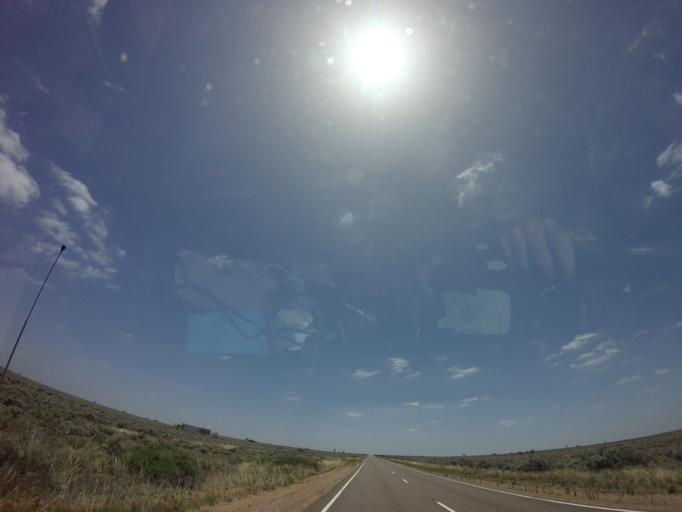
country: AU
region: South Australia
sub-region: Whyalla
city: Whyalla
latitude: -32.8454
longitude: 137.0218
